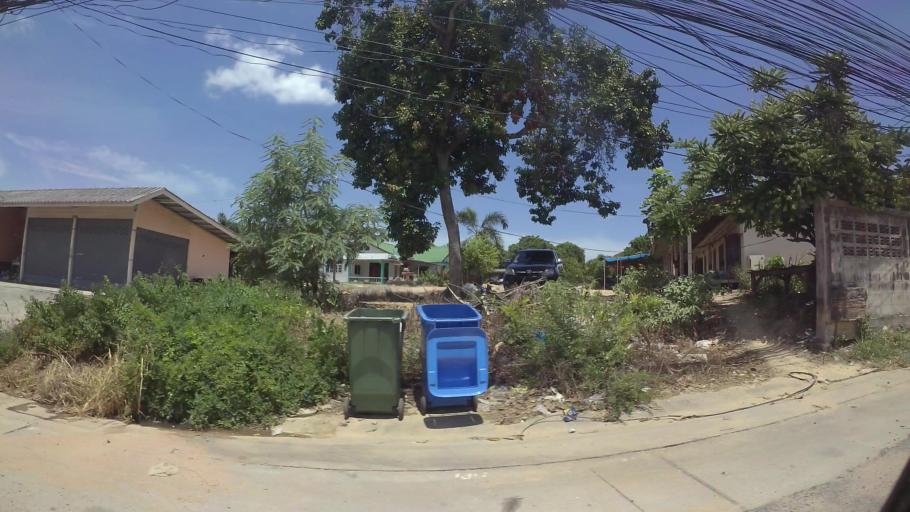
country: TH
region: Chon Buri
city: Ban Talat Bueng
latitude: 13.1158
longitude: 100.9581
